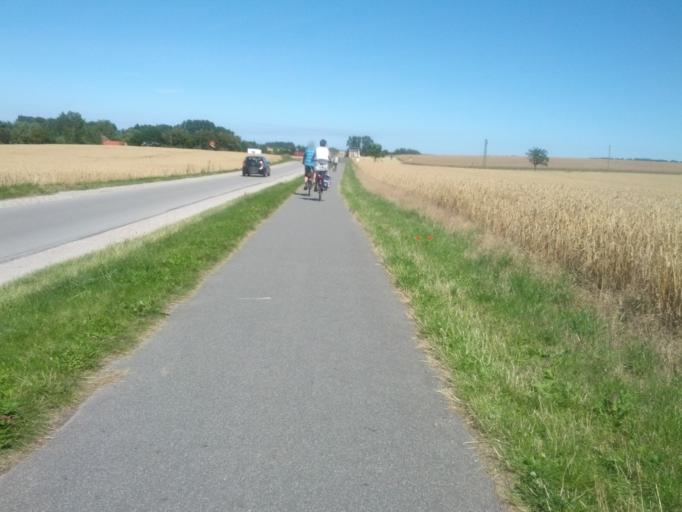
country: DE
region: Mecklenburg-Vorpommern
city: Bastorf
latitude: 54.1219
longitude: 11.6454
